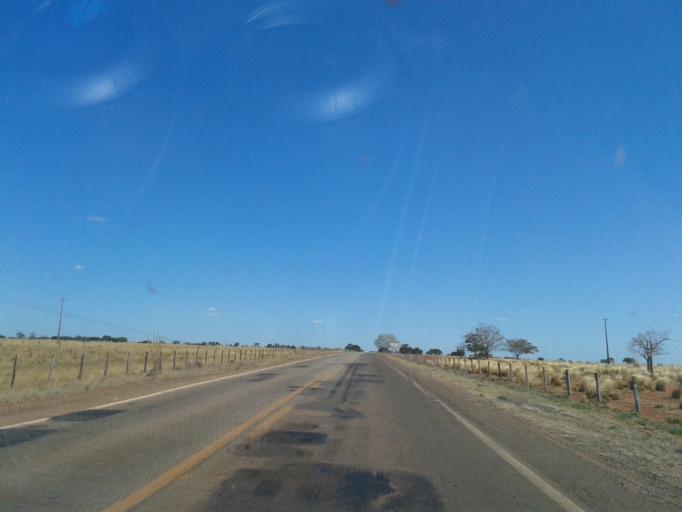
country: BR
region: Goias
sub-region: Crixas
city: Crixas
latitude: -14.1444
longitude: -50.3579
